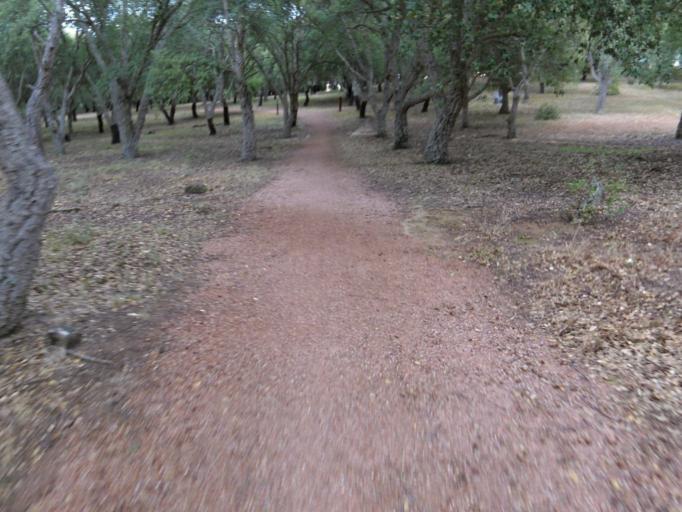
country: AU
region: Australian Capital Territory
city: Macquarie
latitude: -35.2797
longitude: 149.0806
